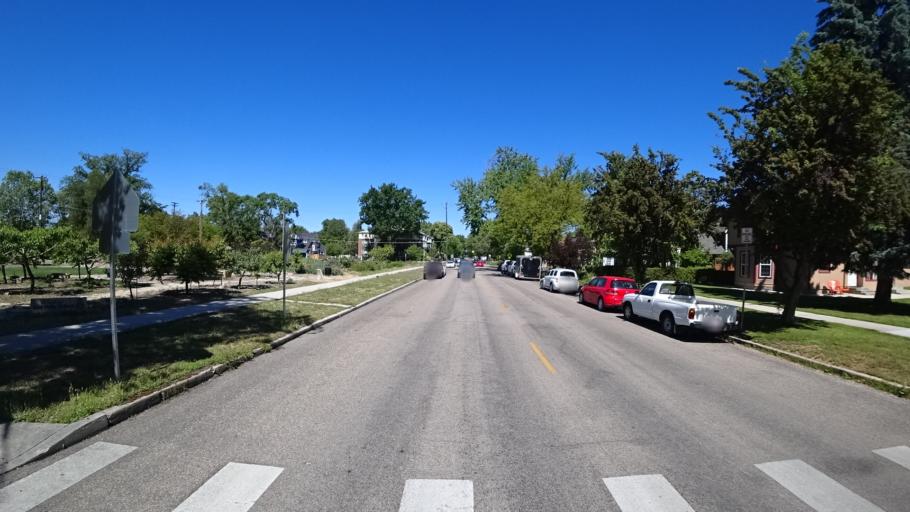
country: US
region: Idaho
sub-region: Ada County
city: Boise
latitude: 43.6235
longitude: -116.2012
